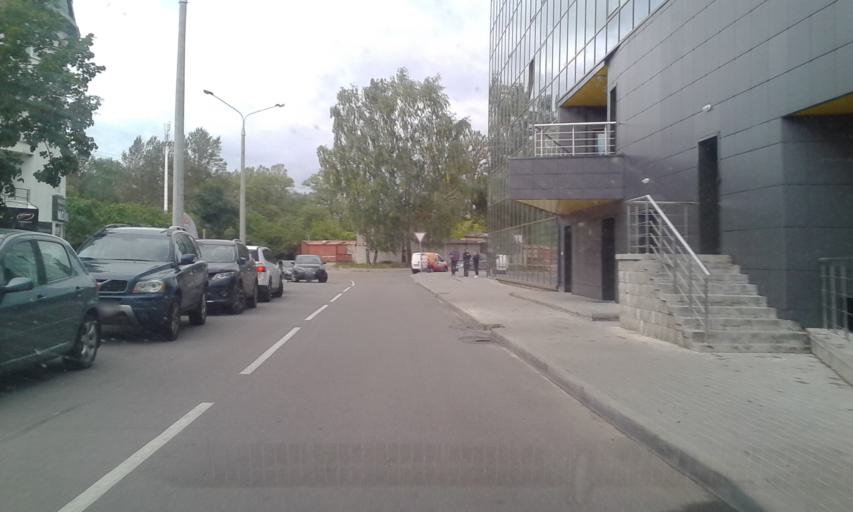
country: BY
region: Minsk
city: Minsk
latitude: 53.9420
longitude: 27.5674
